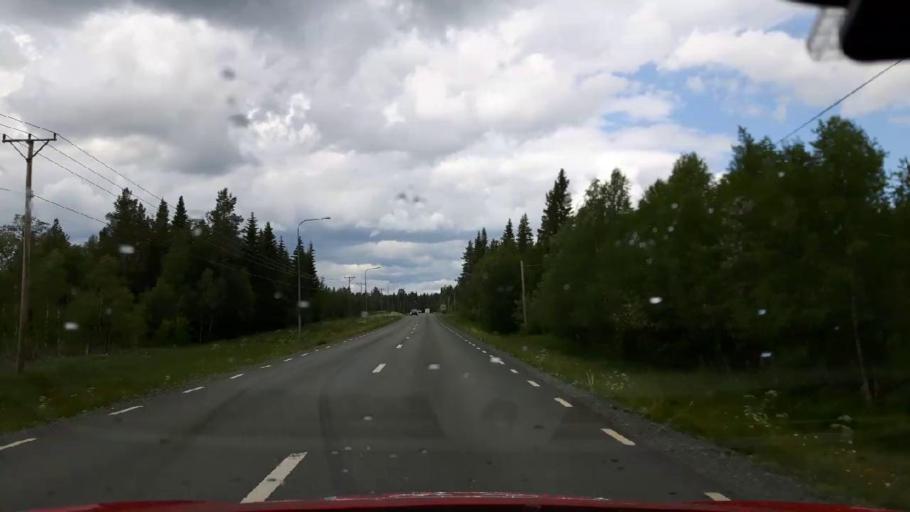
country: SE
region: Jaemtland
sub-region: Krokoms Kommun
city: Krokom
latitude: 63.5575
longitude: 14.2786
